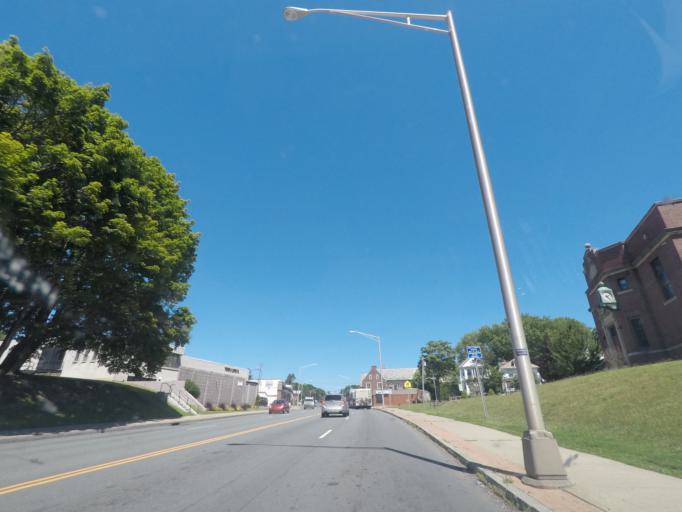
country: US
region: New York
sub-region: Albany County
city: Green Island
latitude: 42.7384
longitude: -73.6609
